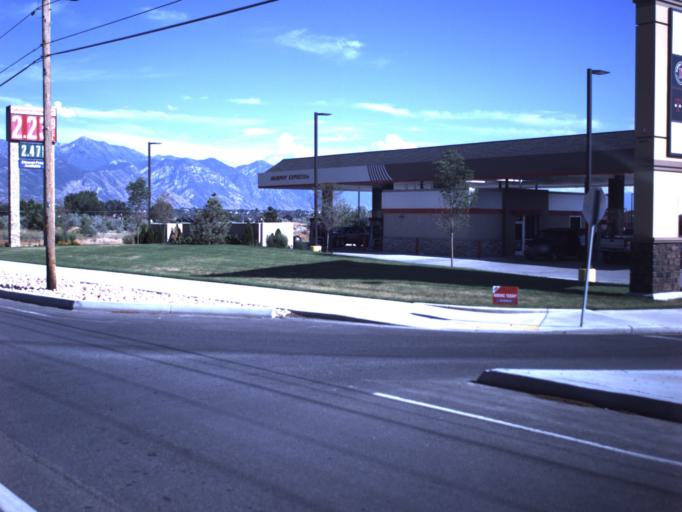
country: US
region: Utah
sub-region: Utah County
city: Pleasant Grove
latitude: 40.3692
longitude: -111.7651
